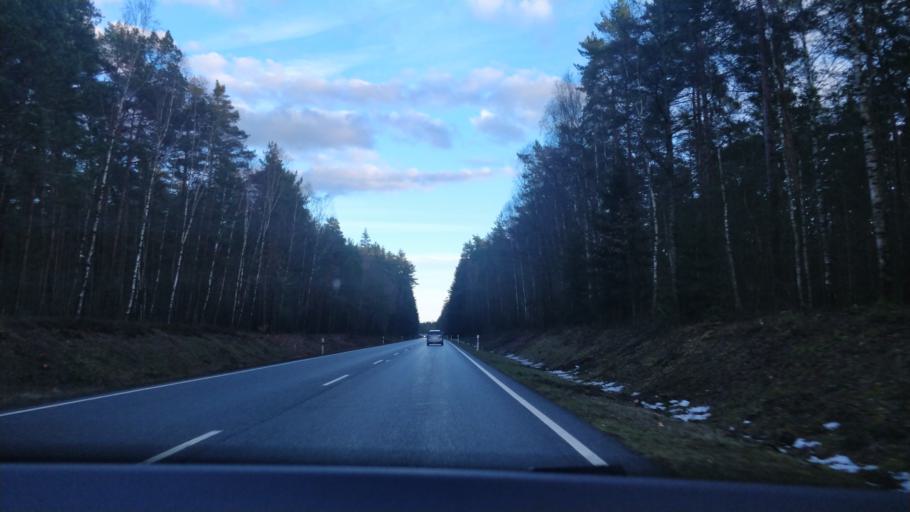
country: DE
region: Bavaria
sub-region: Upper Palatinate
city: Schwarzenbach
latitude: 49.7316
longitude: 11.9586
